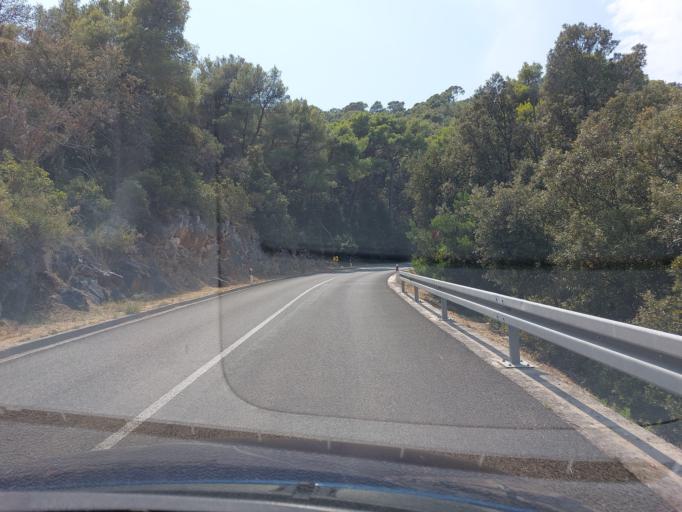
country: HR
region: Dubrovacko-Neretvanska
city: Smokvica
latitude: 42.7675
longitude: 16.8831
